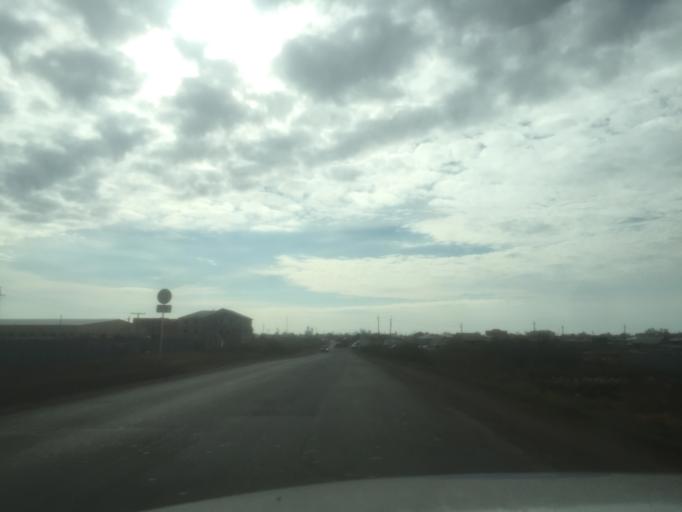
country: KZ
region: Astana Qalasy
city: Astana
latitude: 51.2224
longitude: 71.3882
